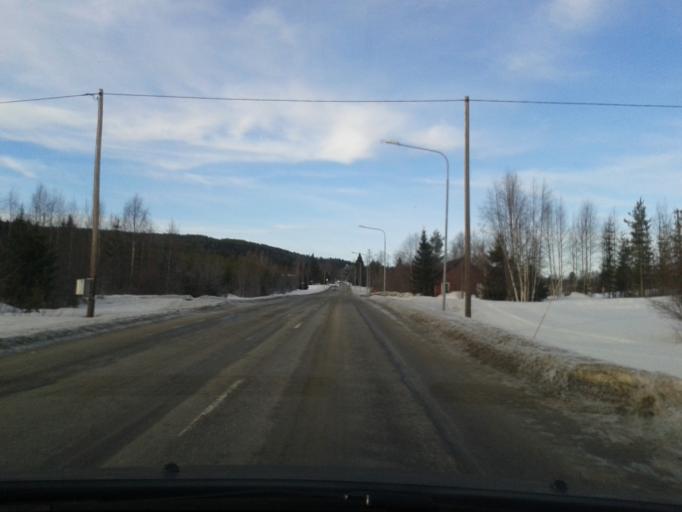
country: SE
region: Vaesternorrland
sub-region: OErnskoeldsviks Kommun
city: Bredbyn
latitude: 63.4824
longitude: 18.0897
